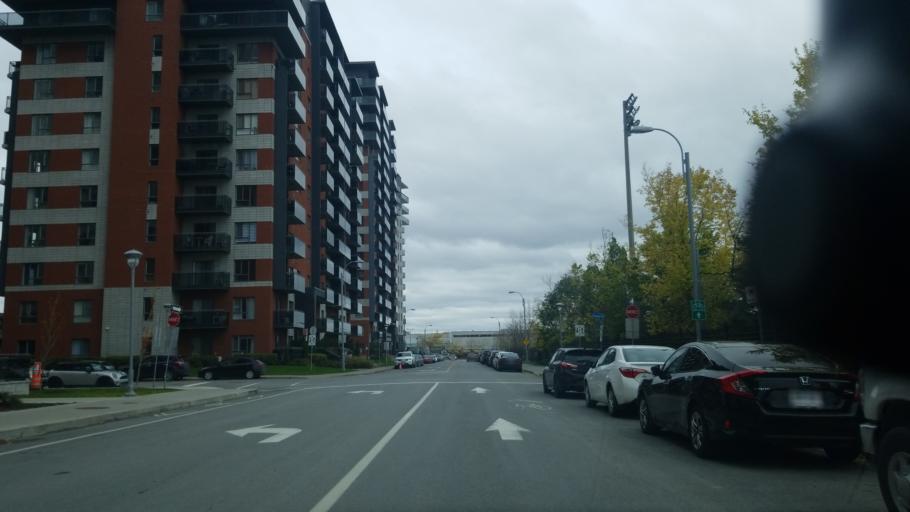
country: CA
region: Quebec
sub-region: Laval
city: Laval
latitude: 45.5596
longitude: -73.7235
